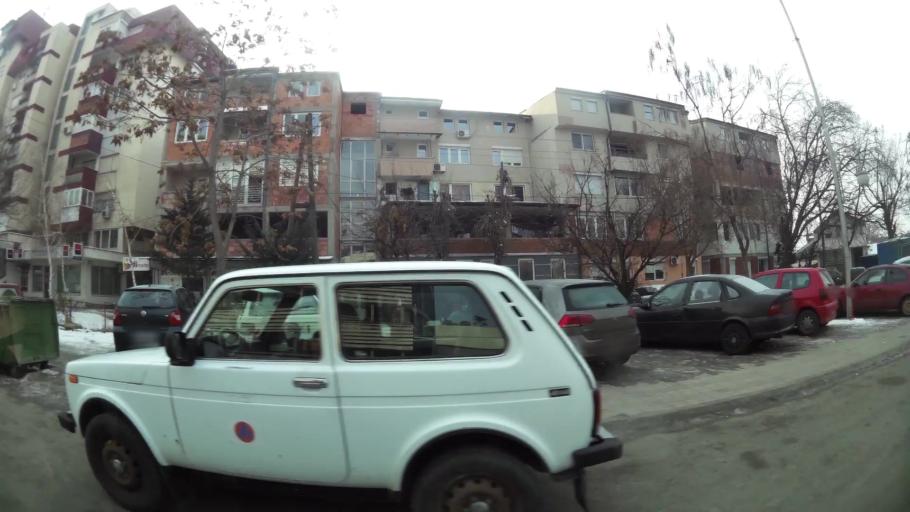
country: MK
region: Cair
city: Cair
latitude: 42.0137
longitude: 21.4424
